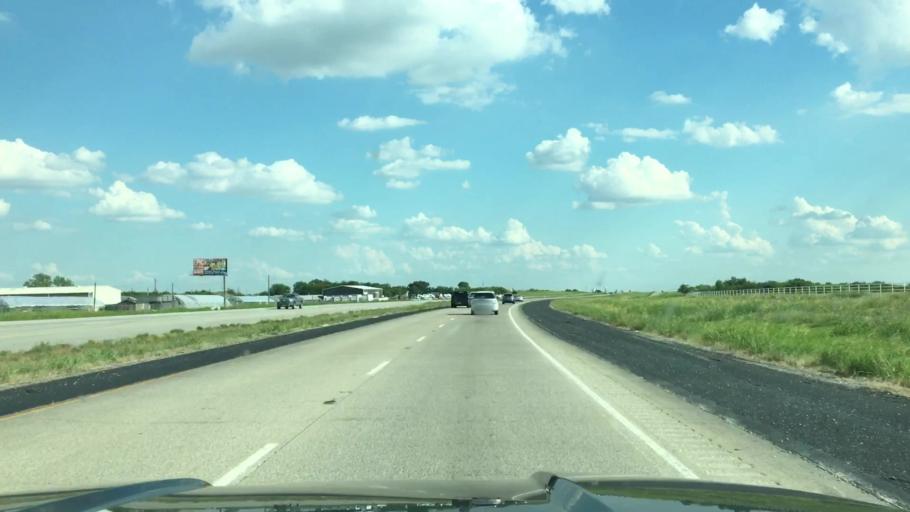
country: US
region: Texas
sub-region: Wise County
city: Rhome
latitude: 33.0238
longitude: -97.4438
